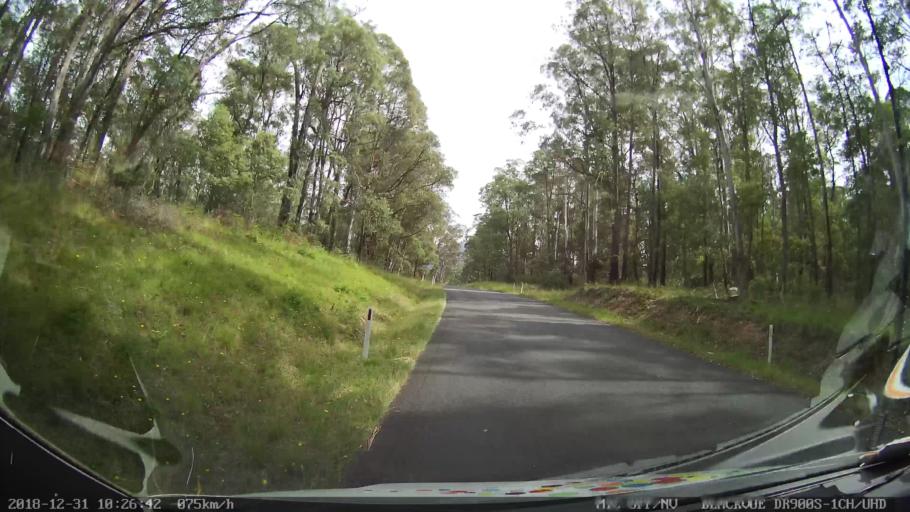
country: AU
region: New South Wales
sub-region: Snowy River
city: Jindabyne
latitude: -36.4925
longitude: 148.1407
